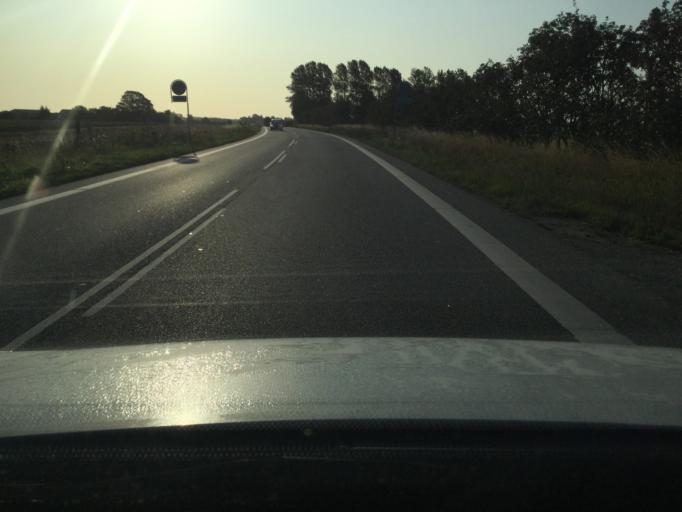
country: DK
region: Zealand
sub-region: Lolland Kommune
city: Nakskov
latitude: 54.8096
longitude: 11.2143
